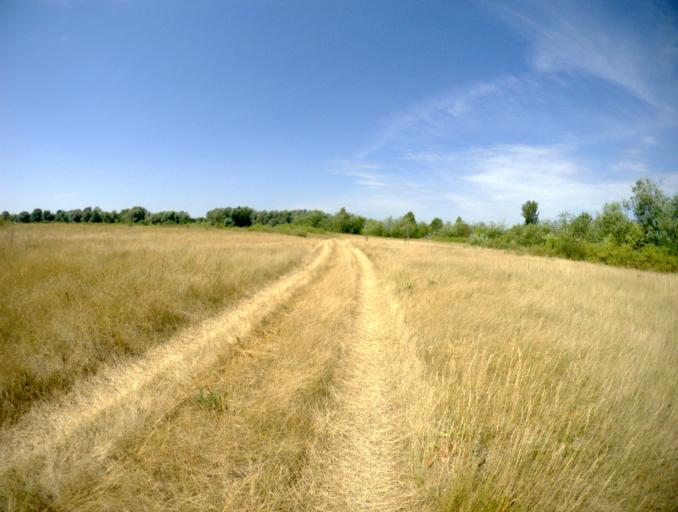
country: RU
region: Vladimir
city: Vorsha
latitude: 56.0419
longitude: 40.1789
